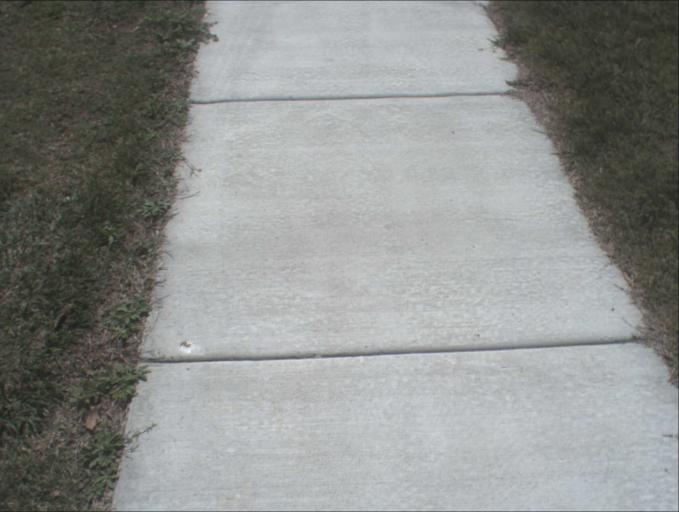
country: AU
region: Queensland
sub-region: Logan
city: Park Ridge South
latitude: -27.7326
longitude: 153.0493
